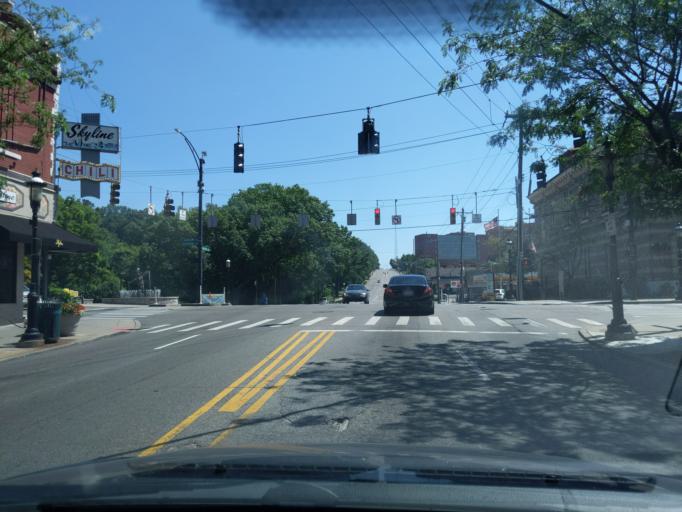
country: US
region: Ohio
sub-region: Hamilton County
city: Saint Bernard
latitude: 39.1437
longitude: -84.5192
